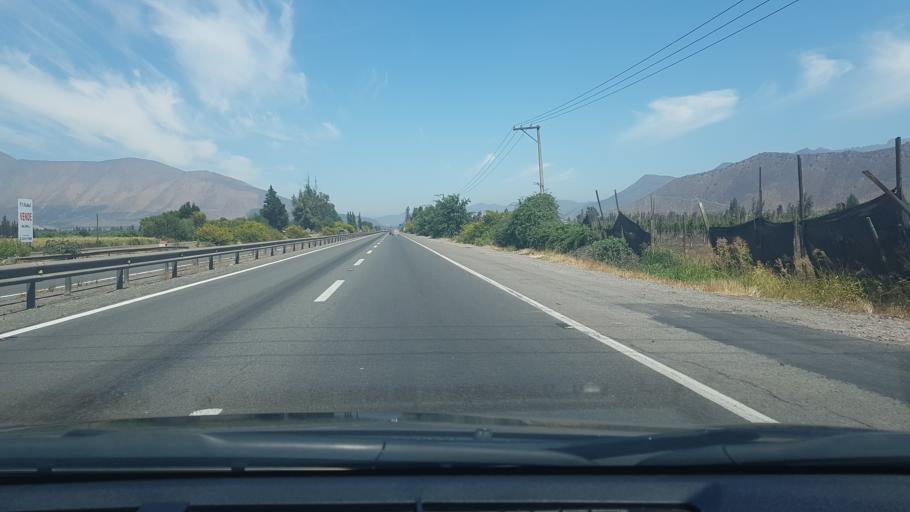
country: CL
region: Valparaiso
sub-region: Provincia de San Felipe
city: Llaillay
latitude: -32.8533
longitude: -70.9279
